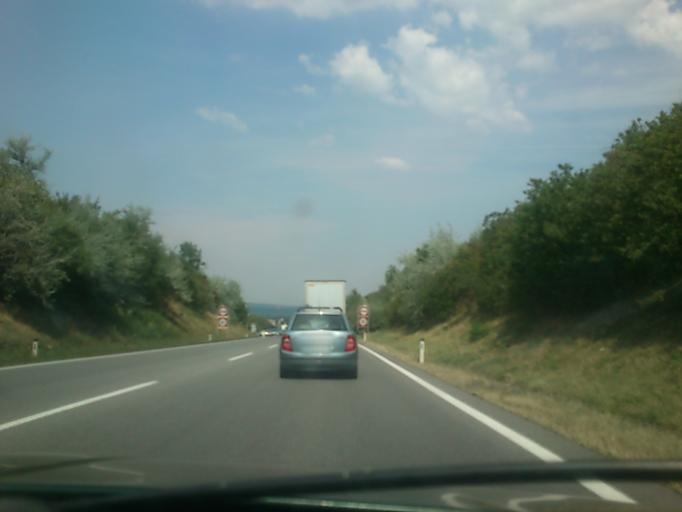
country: AT
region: Lower Austria
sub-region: Politischer Bezirk Mistelbach
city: Drasenhofen
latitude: 48.7380
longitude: 16.6571
